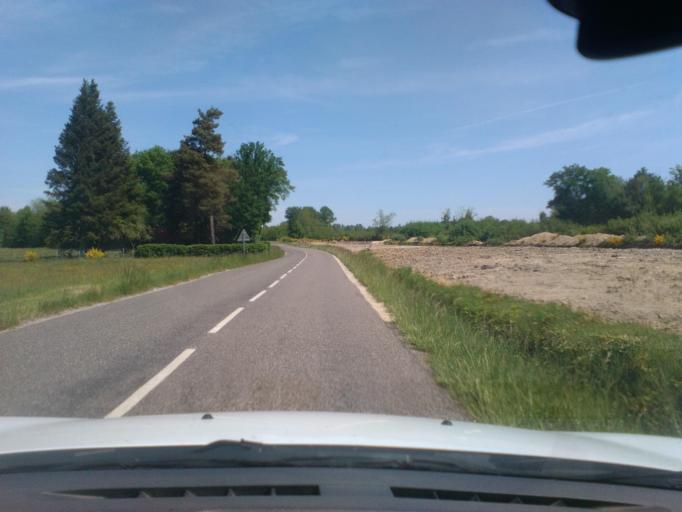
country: FR
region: Lorraine
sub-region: Departement des Vosges
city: Jeanmenil
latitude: 48.3072
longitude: 6.6827
